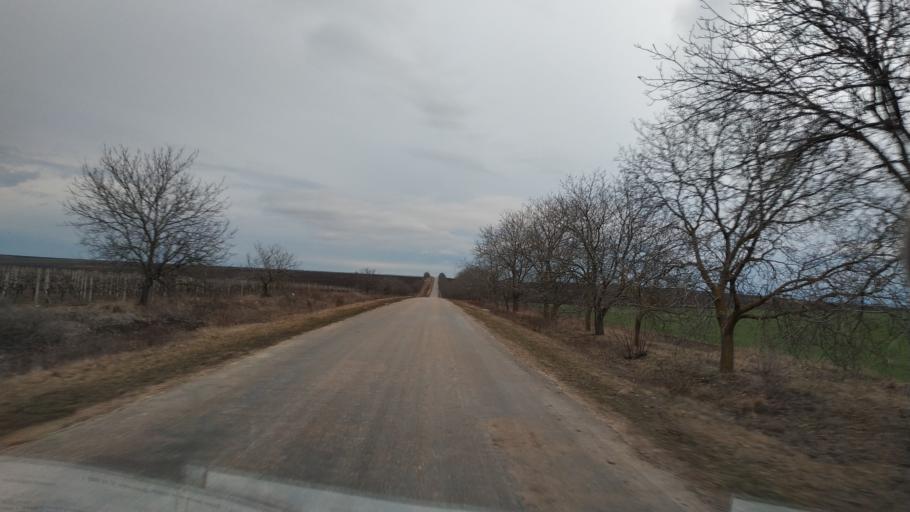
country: MD
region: Causeni
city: Causeni
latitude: 46.6076
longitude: 29.4013
